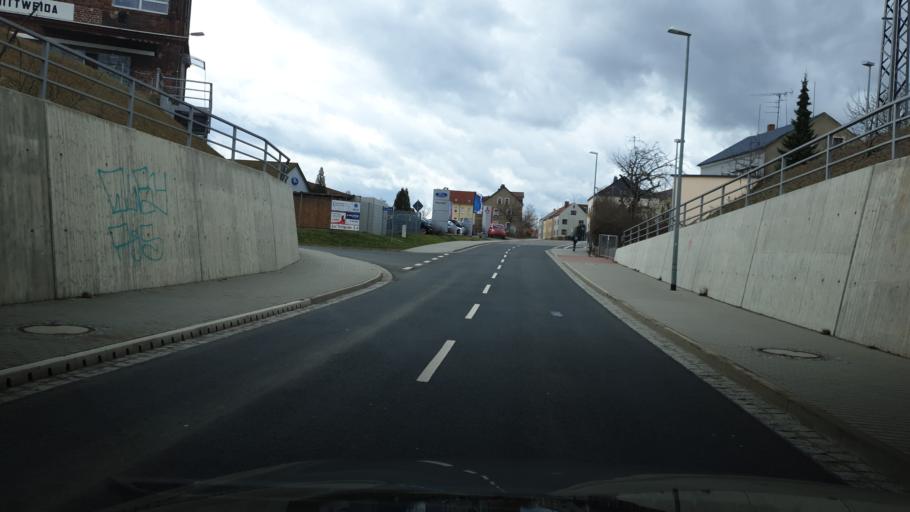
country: DE
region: Saxony
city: Mittweida
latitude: 50.9856
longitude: 12.9598
